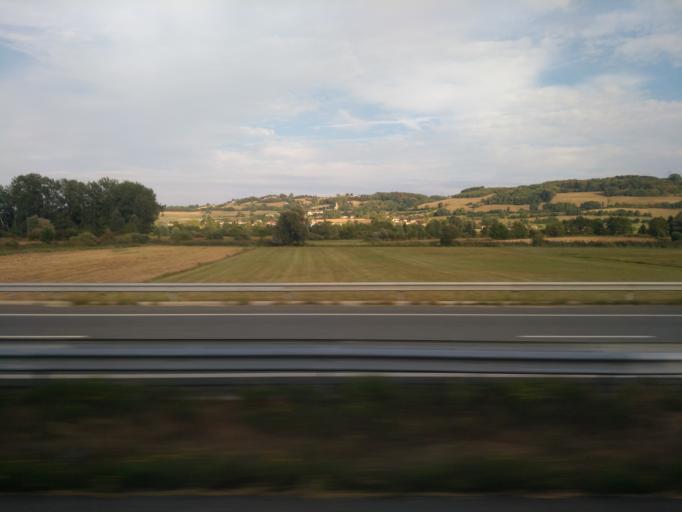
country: FR
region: Rhone-Alpes
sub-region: Departement de l'Isere
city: Saint-Victor-de-Cessieu
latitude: 45.5005
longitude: 5.3993
